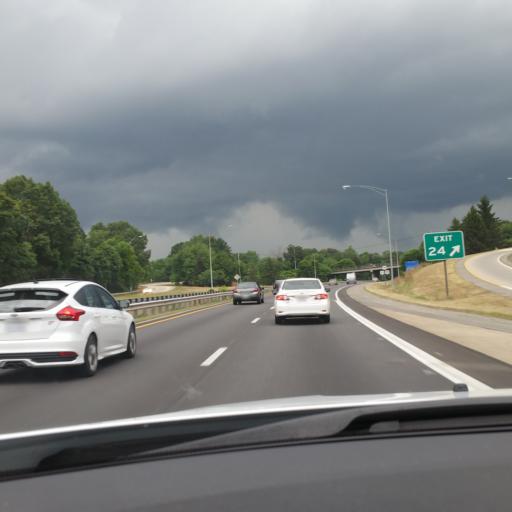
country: US
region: North Carolina
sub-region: Buncombe County
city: Woodfin
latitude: 35.6282
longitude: -82.5798
